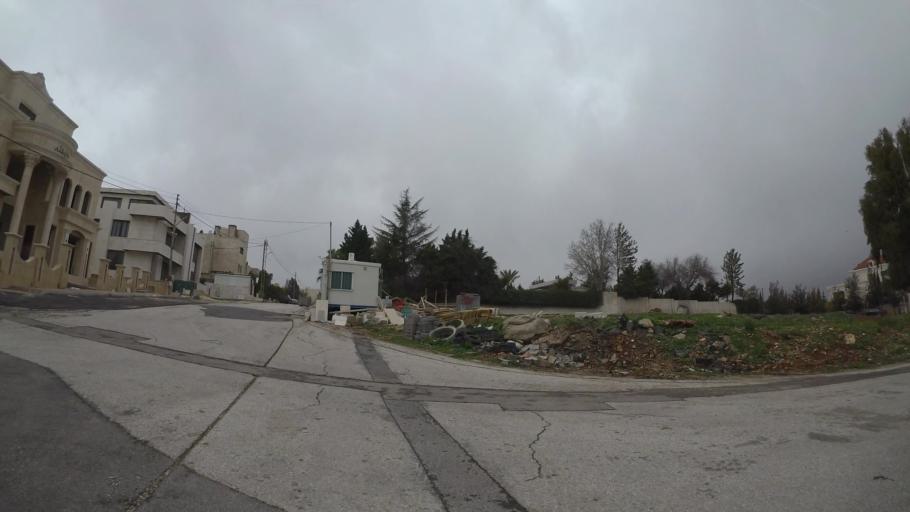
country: JO
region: Amman
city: Al Bunayyat ash Shamaliyah
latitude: 31.9366
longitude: 35.8846
